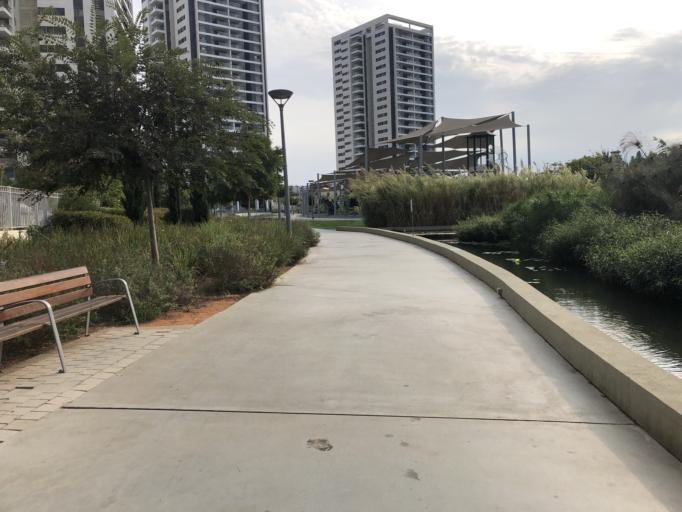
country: IL
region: Tel Aviv
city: Giv`at Shemu'el
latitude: 32.0564
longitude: 34.8452
